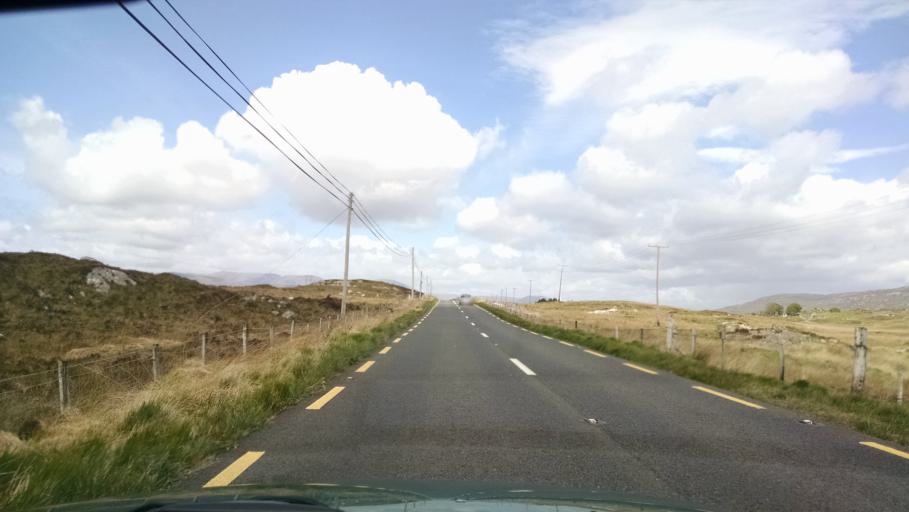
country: IE
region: Connaught
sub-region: County Galway
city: Oughterard
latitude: 53.3541
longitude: -9.5422
